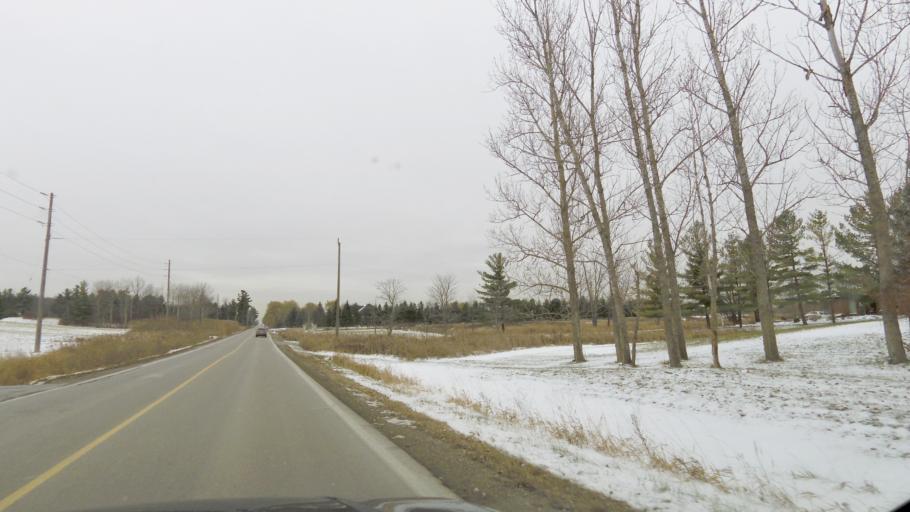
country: CA
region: Ontario
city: Vaughan
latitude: 43.8749
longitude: -79.5944
